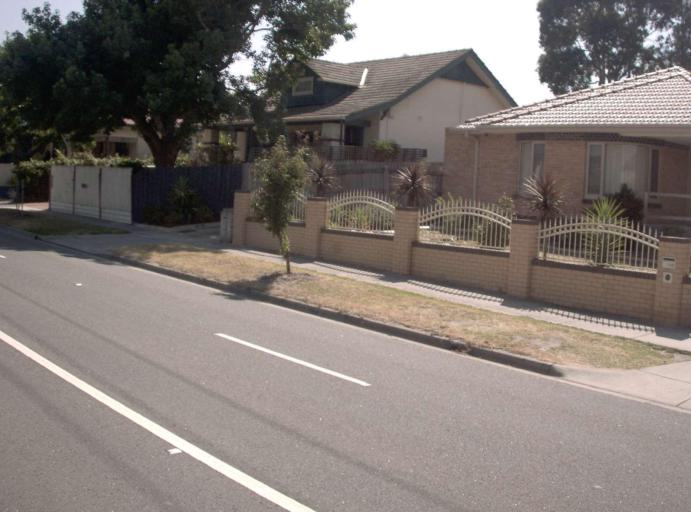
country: AU
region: Victoria
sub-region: Kingston
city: Mentone
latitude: -37.9792
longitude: 145.0719
